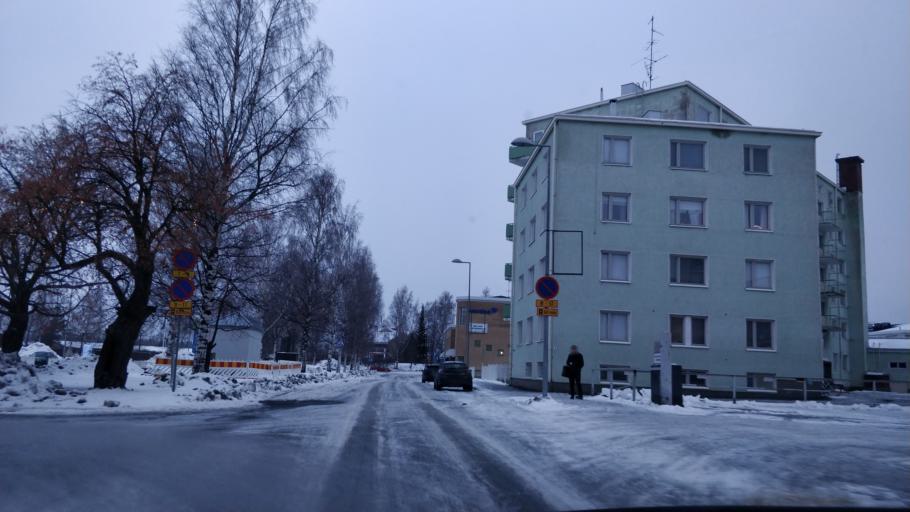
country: FI
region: Lapland
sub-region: Kemi-Tornio
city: Kemi
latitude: 65.7377
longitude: 24.5617
